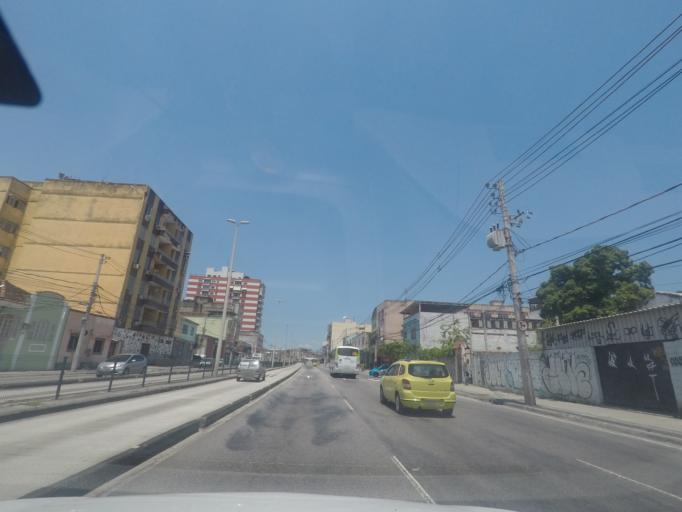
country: BR
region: Rio de Janeiro
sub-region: Duque De Caxias
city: Duque de Caxias
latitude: -22.8383
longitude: -43.2933
